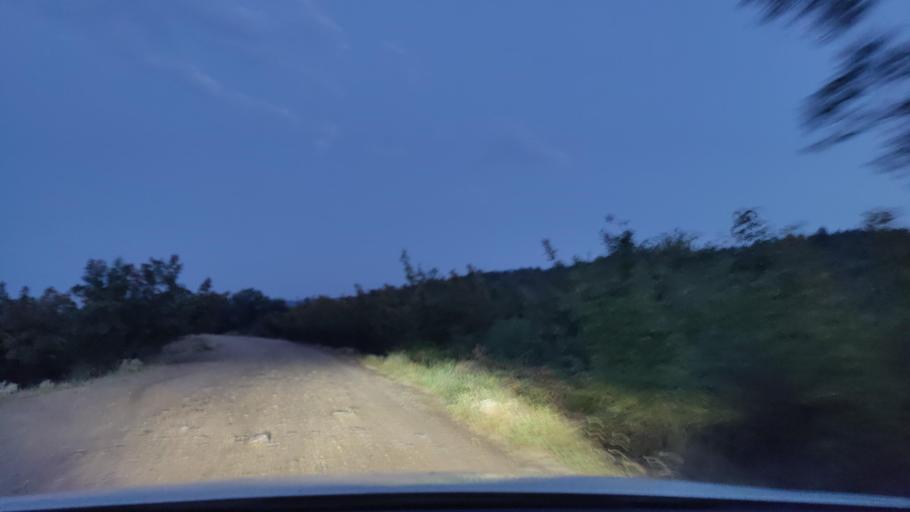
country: GR
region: Central Macedonia
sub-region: Nomos Serron
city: Chrysochorafa
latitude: 41.2012
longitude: 23.0821
